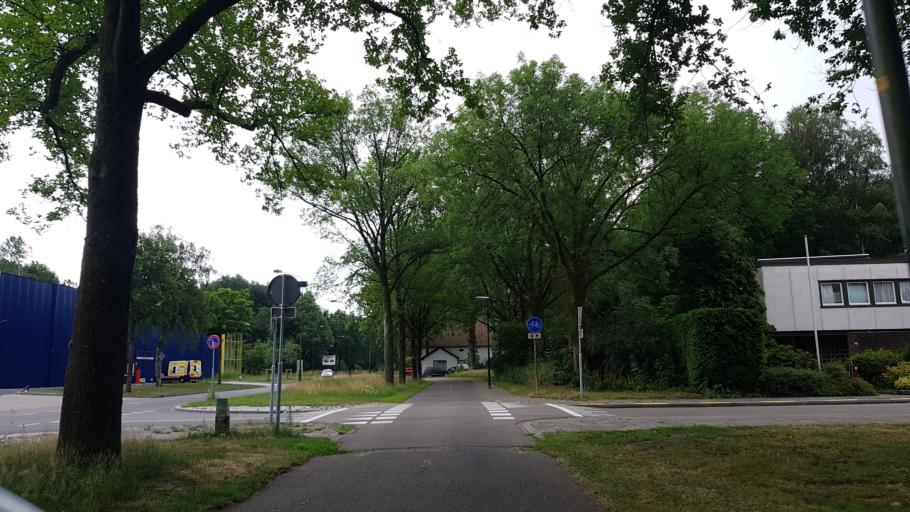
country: NL
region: Gelderland
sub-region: Gemeente Apeldoorn
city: Apeldoorn
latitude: 52.1873
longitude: 5.9813
